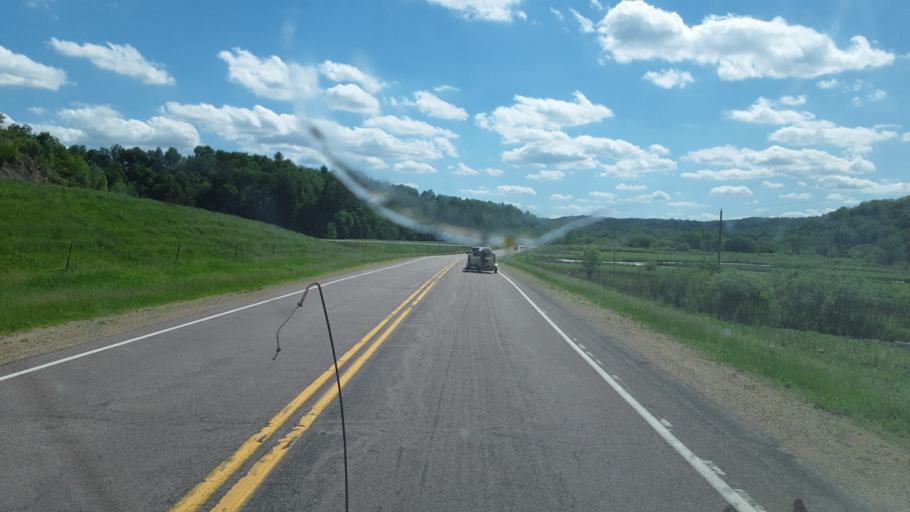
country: US
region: Wisconsin
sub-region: Richland County
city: Richland Center
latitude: 43.3851
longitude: -90.2498
